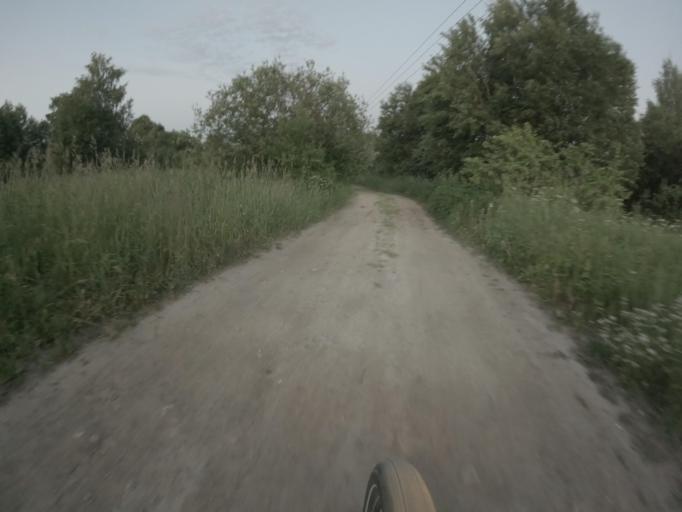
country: RU
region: Leningrad
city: Imeni Sverdlova
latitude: 59.7814
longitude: 30.6878
